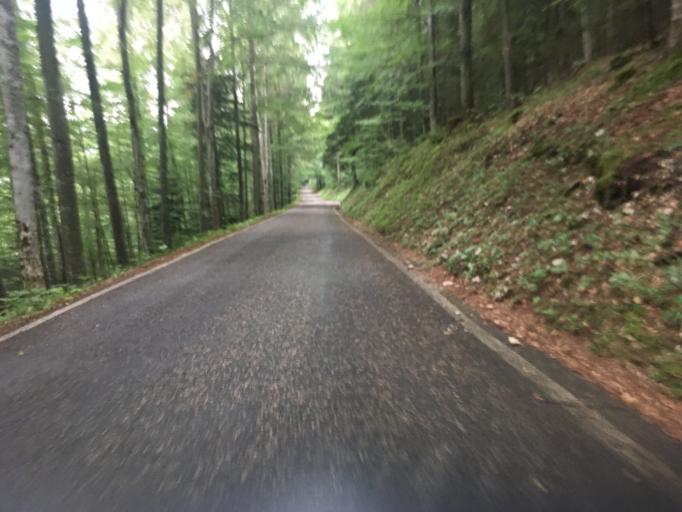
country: CH
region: Solothurn
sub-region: Bezirk Thal
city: Welschenrohr
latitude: 47.2558
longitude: 7.4996
